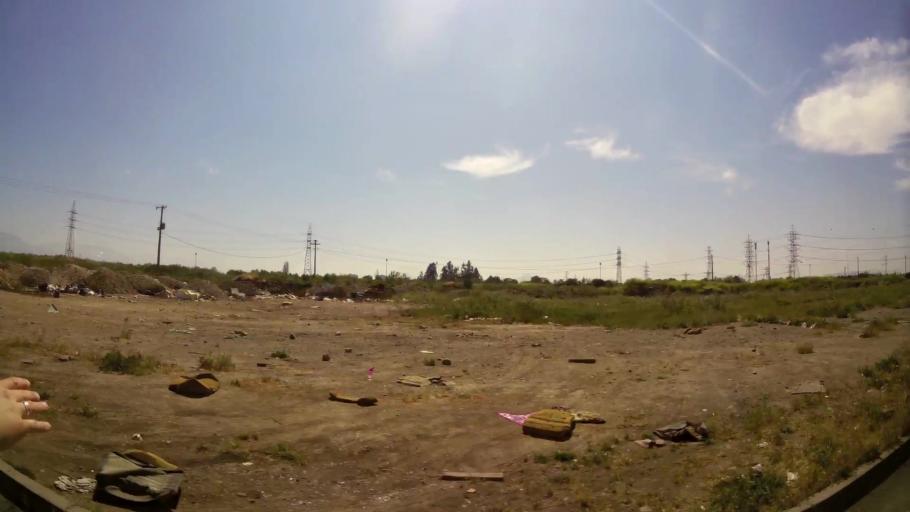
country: CL
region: Santiago Metropolitan
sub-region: Provincia de Santiago
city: Lo Prado
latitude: -33.4853
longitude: -70.7332
